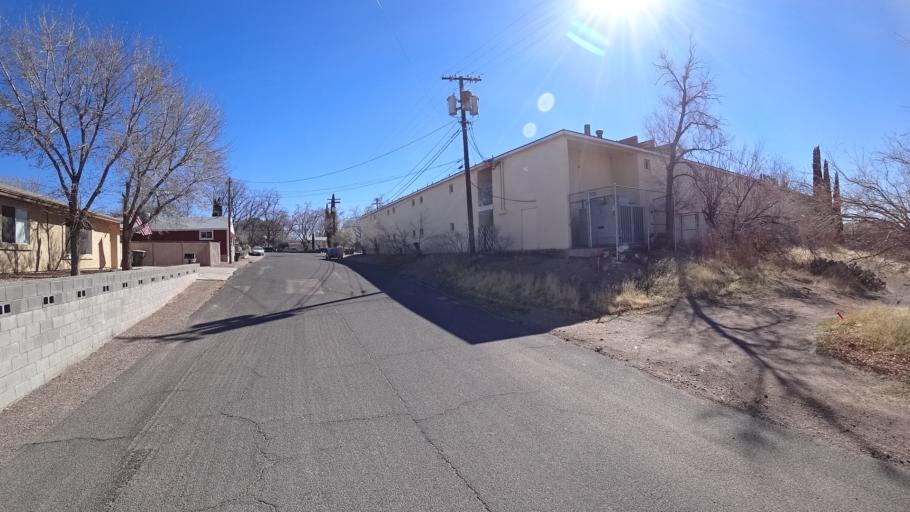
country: US
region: Arizona
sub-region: Mohave County
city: Kingman
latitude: 35.1912
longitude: -114.0623
